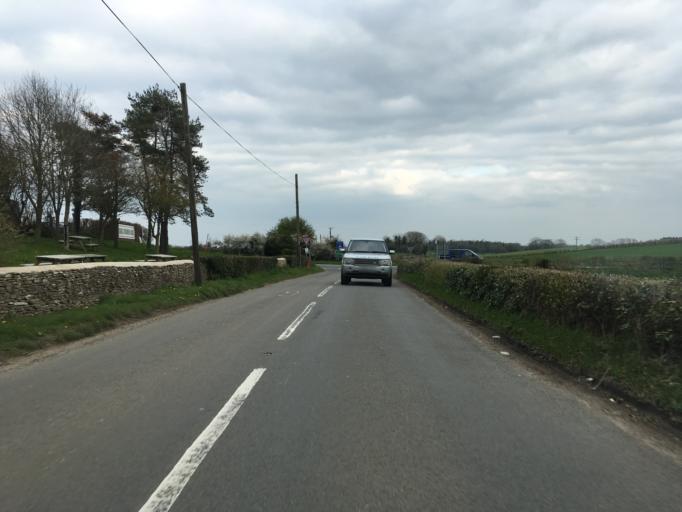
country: GB
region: England
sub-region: Wiltshire
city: Hankerton
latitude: 51.6554
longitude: -2.0547
